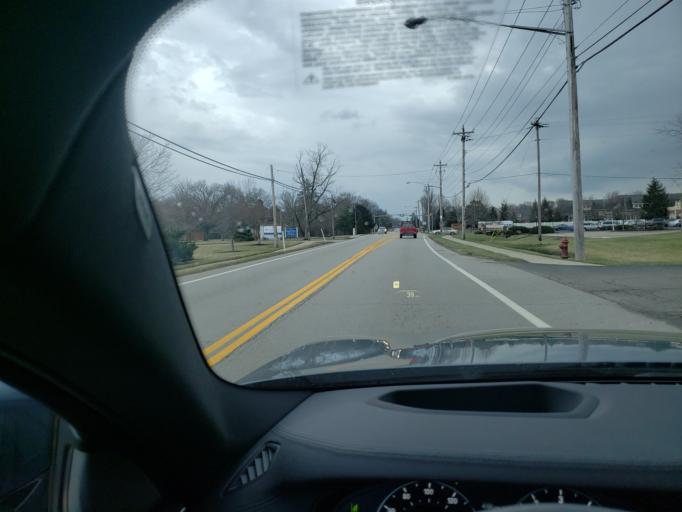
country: US
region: Ohio
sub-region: Hamilton County
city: Springdale
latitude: 39.2797
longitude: -84.4838
